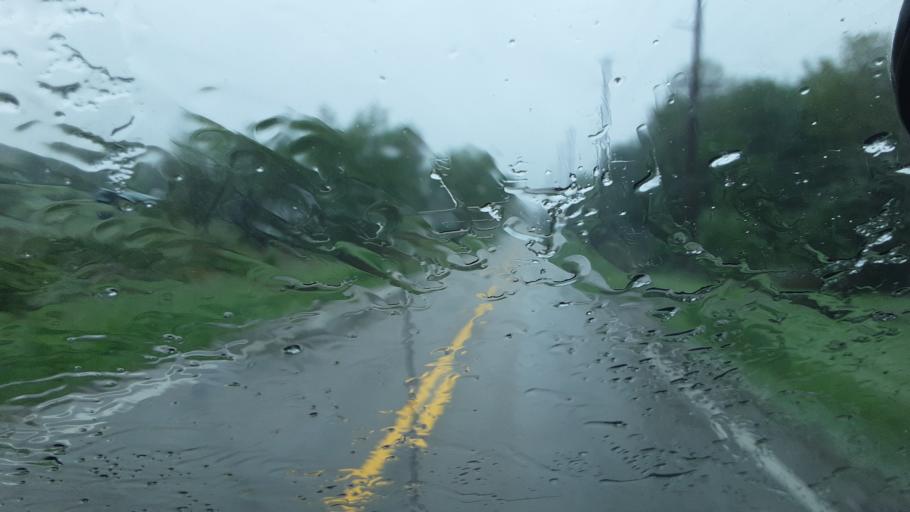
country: US
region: Ohio
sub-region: Portage County
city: Windham
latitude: 41.3084
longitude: -80.9798
